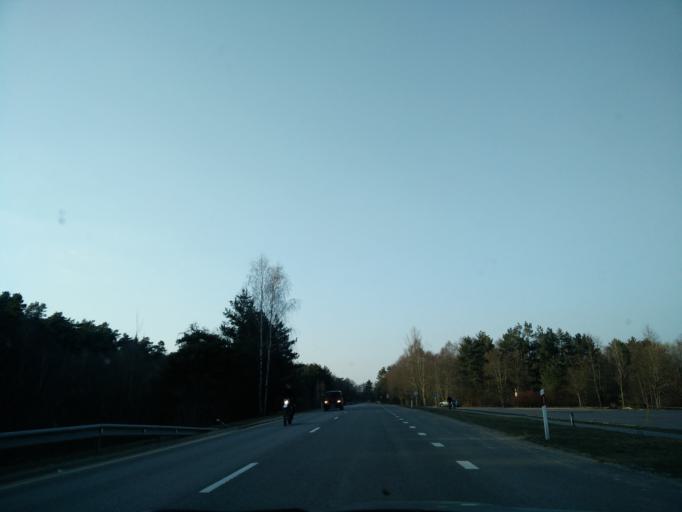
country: LT
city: Trakai
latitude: 54.6578
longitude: 24.9161
